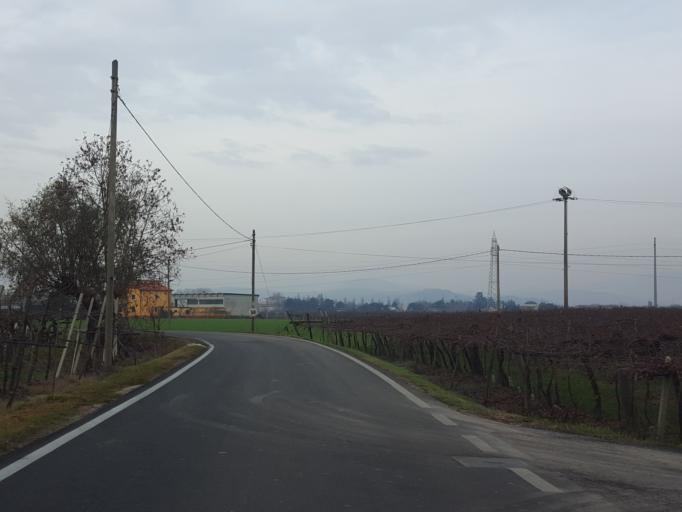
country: IT
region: Veneto
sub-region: Provincia di Verona
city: San Bonifacio
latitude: 45.3853
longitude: 11.2860
